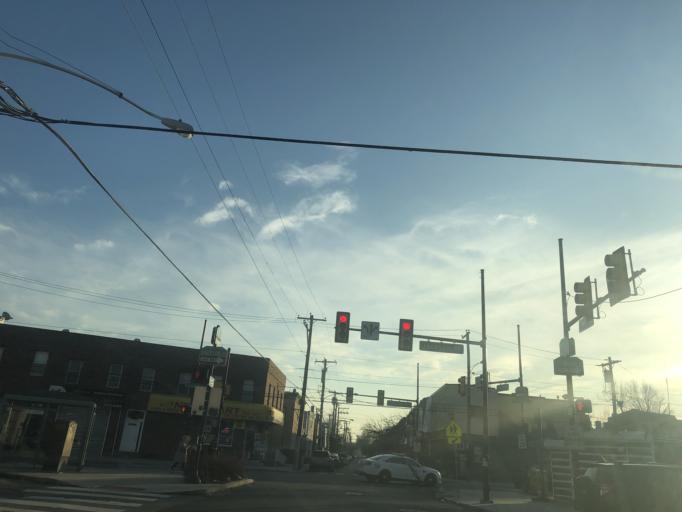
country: US
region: Pennsylvania
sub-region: Philadelphia County
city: Philadelphia
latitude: 39.9244
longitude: -75.1779
